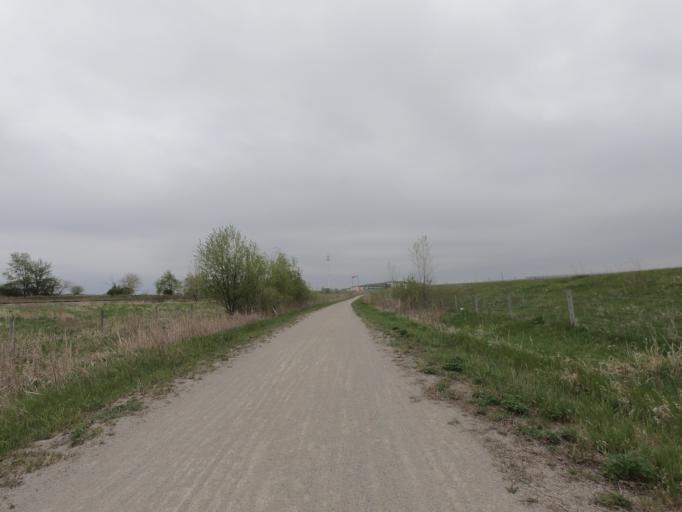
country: US
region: Wisconsin
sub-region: Jefferson County
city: Jefferson
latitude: 43.0361
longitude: -88.8034
